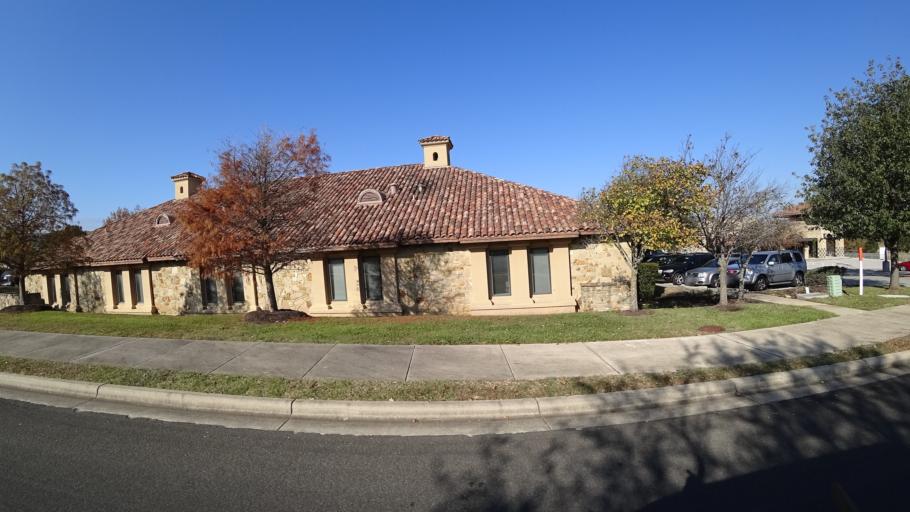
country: US
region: Texas
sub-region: Williamson County
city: Anderson Mill
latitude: 30.3920
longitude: -97.8423
